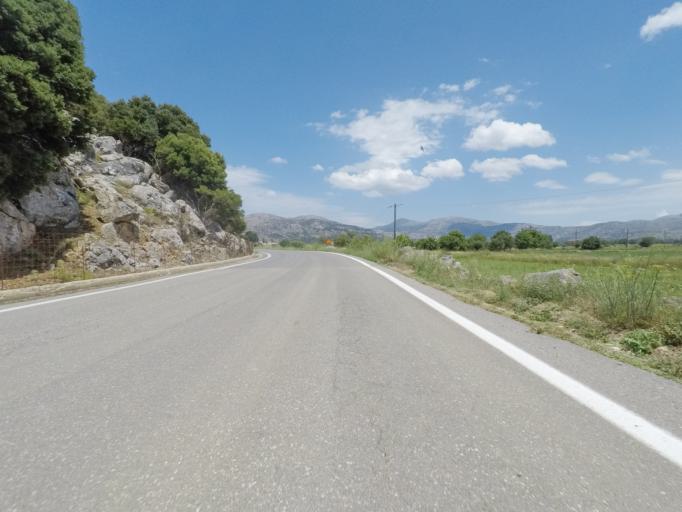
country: GR
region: Crete
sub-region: Nomos Irakleiou
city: Mokhos
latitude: 35.1957
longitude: 25.4584
